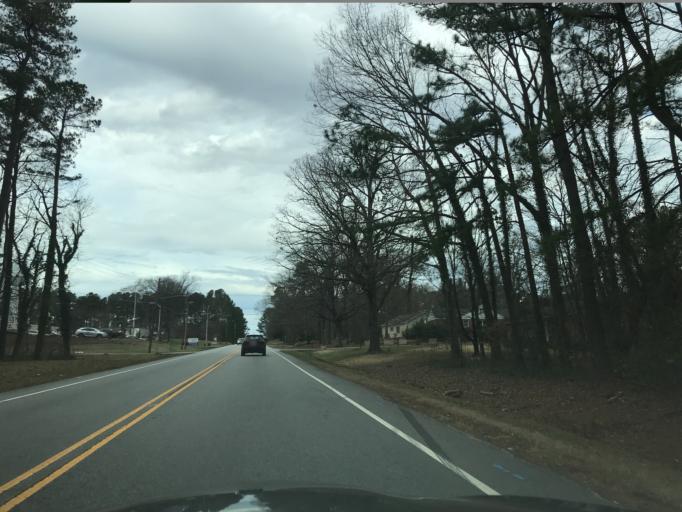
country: US
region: North Carolina
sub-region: Franklin County
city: Louisburg
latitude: 36.1113
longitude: -78.2921
